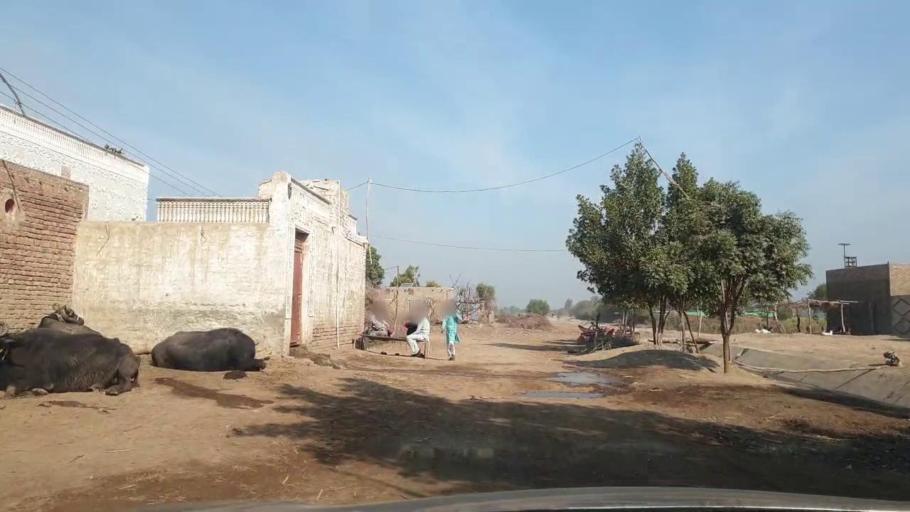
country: PK
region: Sindh
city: Tando Allahyar
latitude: 25.6028
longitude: 68.7222
